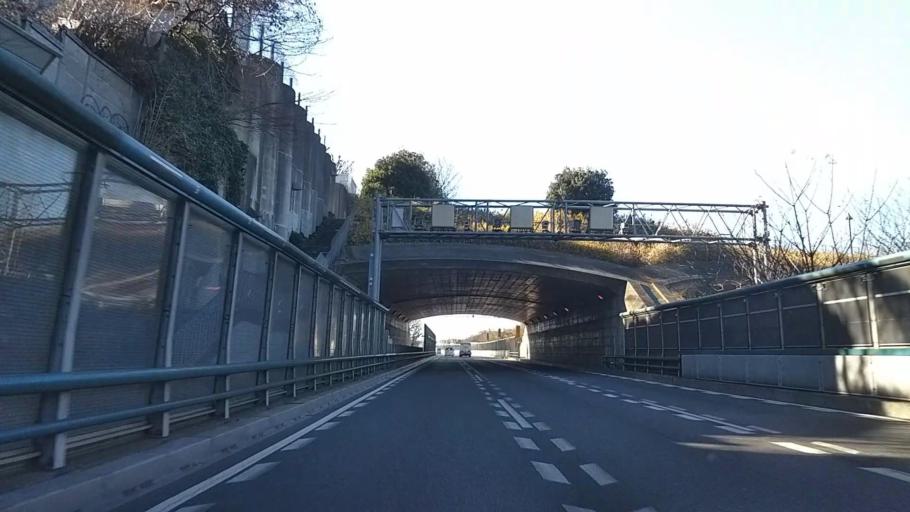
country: JP
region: Kanagawa
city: Yokohama
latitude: 35.4691
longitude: 139.5686
